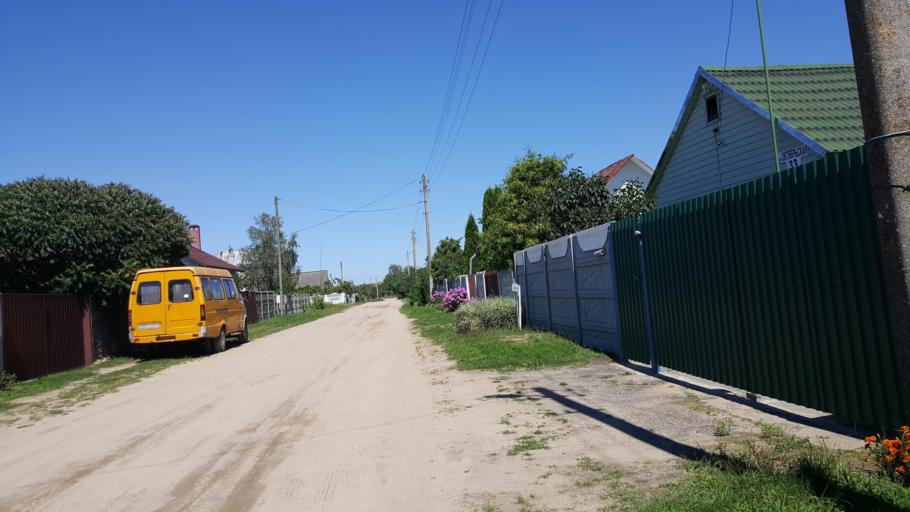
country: BY
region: Brest
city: Charnawchytsy
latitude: 52.2310
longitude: 23.7796
